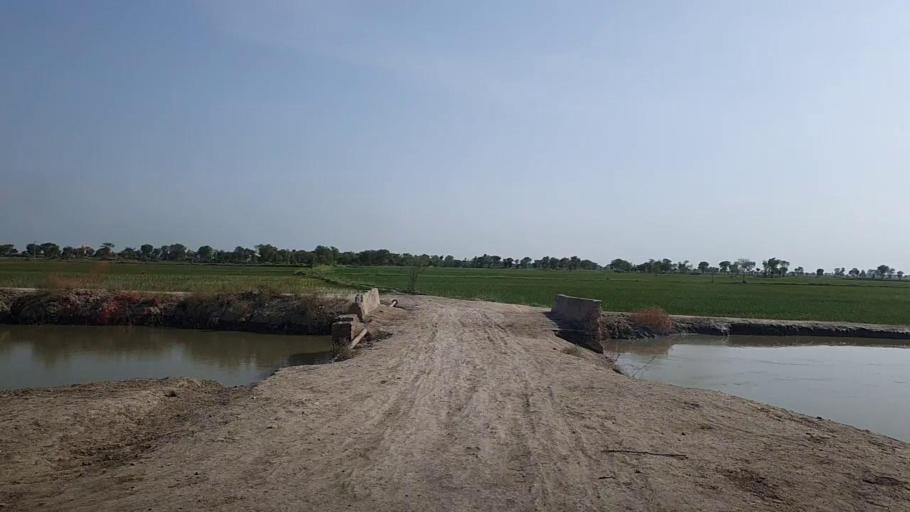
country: PK
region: Sindh
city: Sita Road
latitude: 27.0917
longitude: 67.8478
